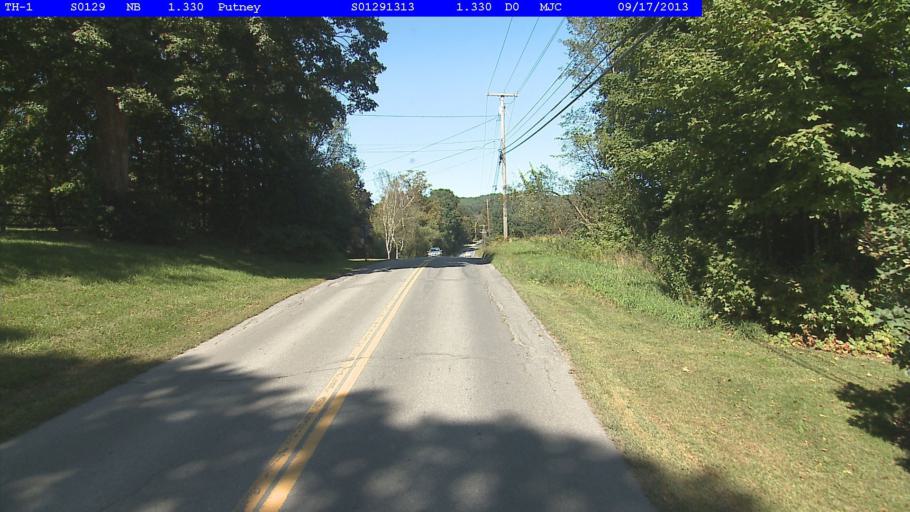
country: US
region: New Hampshire
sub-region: Cheshire County
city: Westmoreland
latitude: 42.9918
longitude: -72.5314
